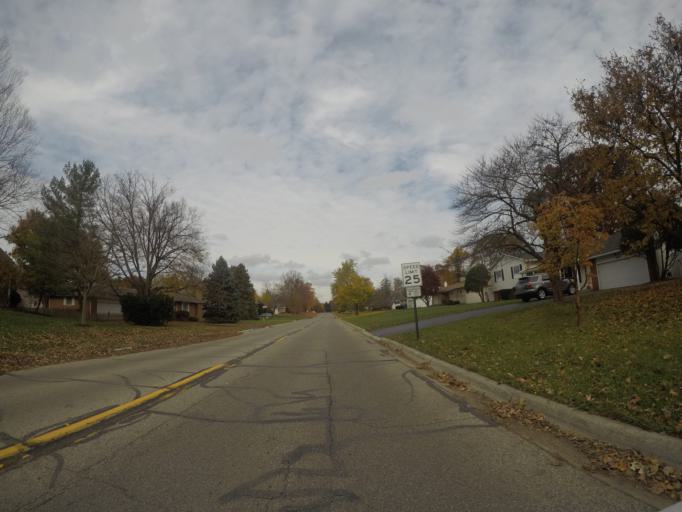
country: US
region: Ohio
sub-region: Franklin County
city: Upper Arlington
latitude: 40.0194
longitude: -83.0477
